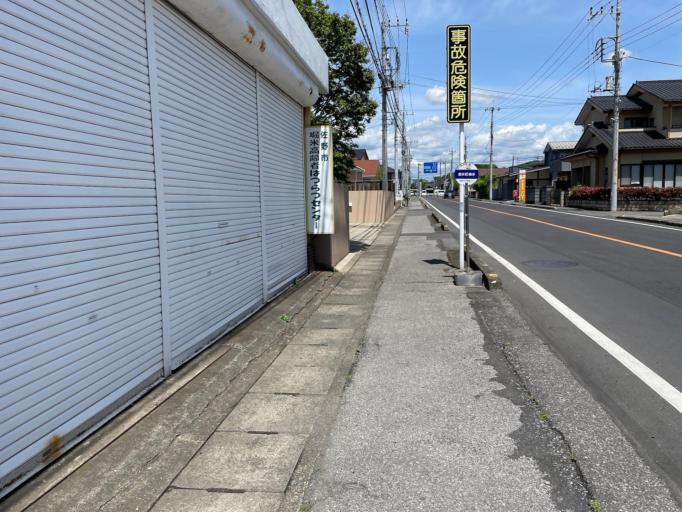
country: JP
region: Tochigi
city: Sano
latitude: 36.3205
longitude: 139.5847
